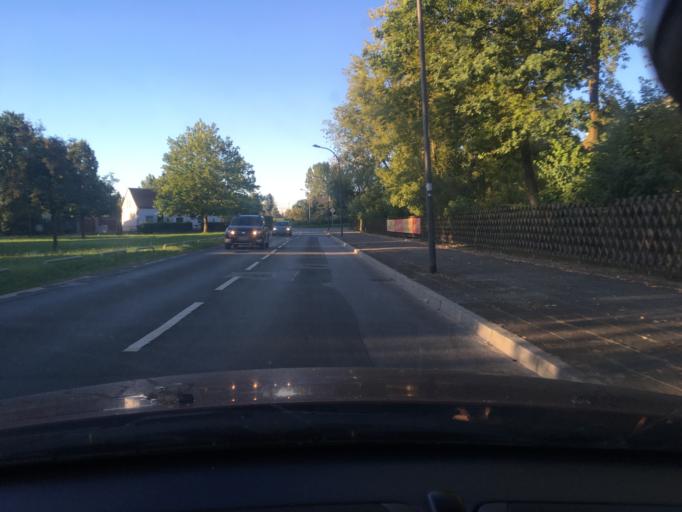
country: DE
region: Saxony
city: Goerlitz
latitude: 51.1425
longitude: 14.9480
